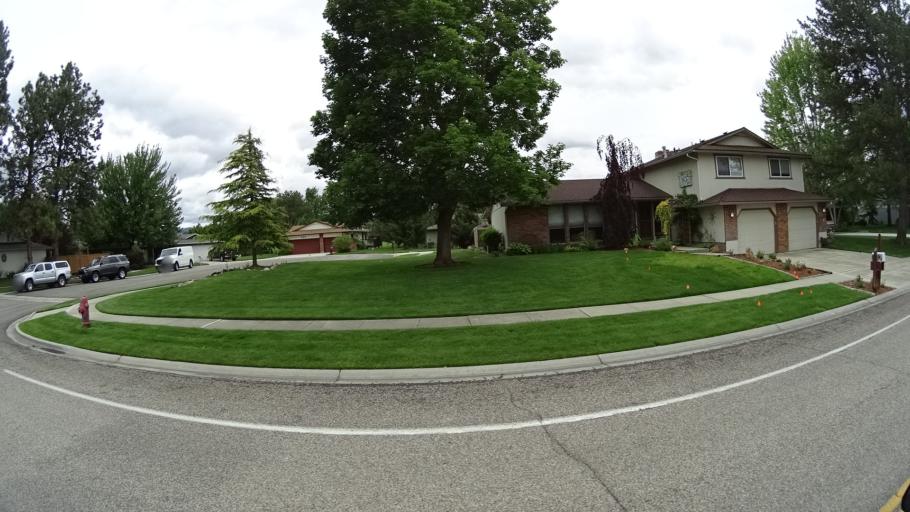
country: US
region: Idaho
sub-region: Ada County
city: Eagle
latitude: 43.7031
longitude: -116.3435
